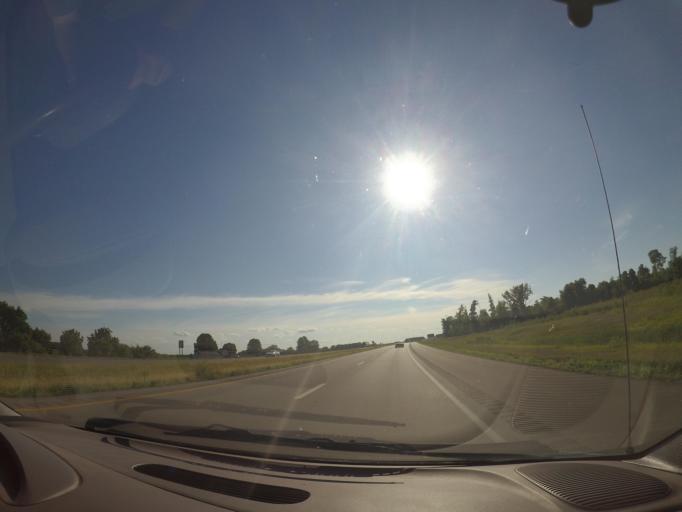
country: US
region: Ohio
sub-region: Henry County
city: Liberty Center
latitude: 41.4292
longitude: -83.9930
